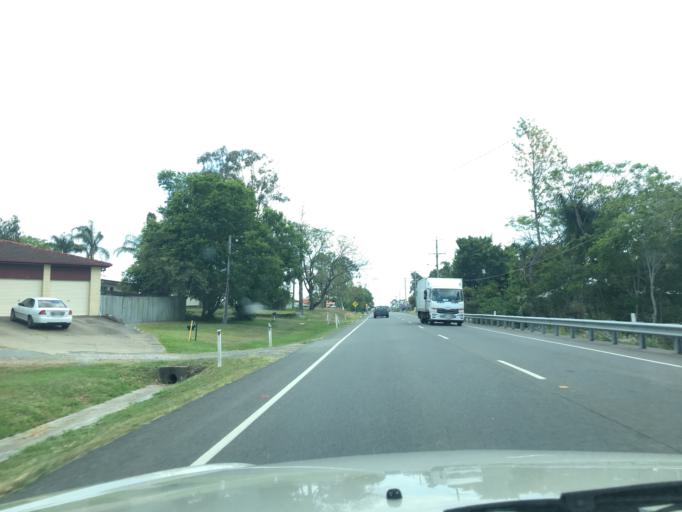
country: AU
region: Queensland
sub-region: Logan
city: Waterford West
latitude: -27.6983
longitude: 153.1461
